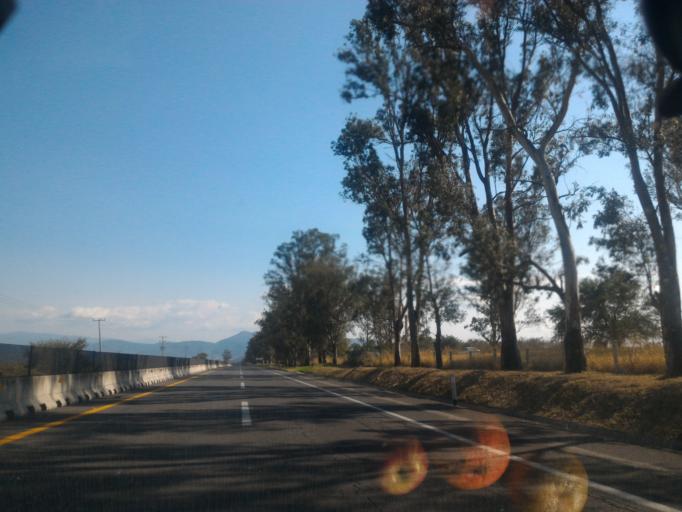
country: MX
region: Jalisco
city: Zapotiltic
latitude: 19.5686
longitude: -103.4435
